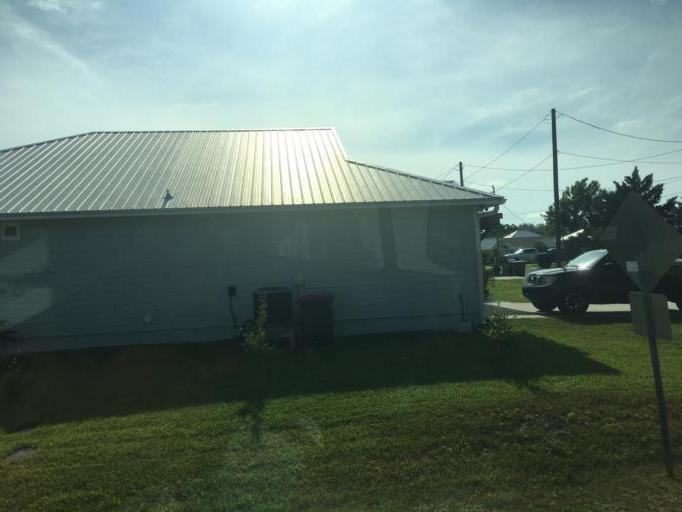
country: US
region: Florida
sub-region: Bay County
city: Laguna Beach
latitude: 30.2548
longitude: -85.9499
